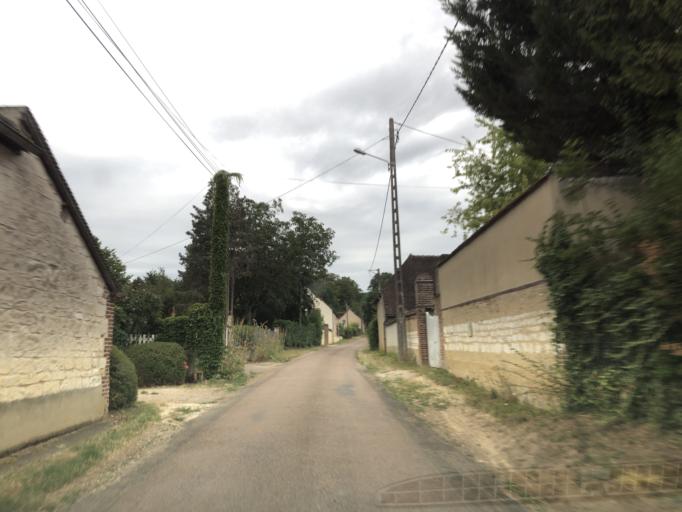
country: FR
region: Bourgogne
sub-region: Departement de l'Yonne
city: Aillant-sur-Tholon
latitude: 47.9040
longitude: 3.3265
